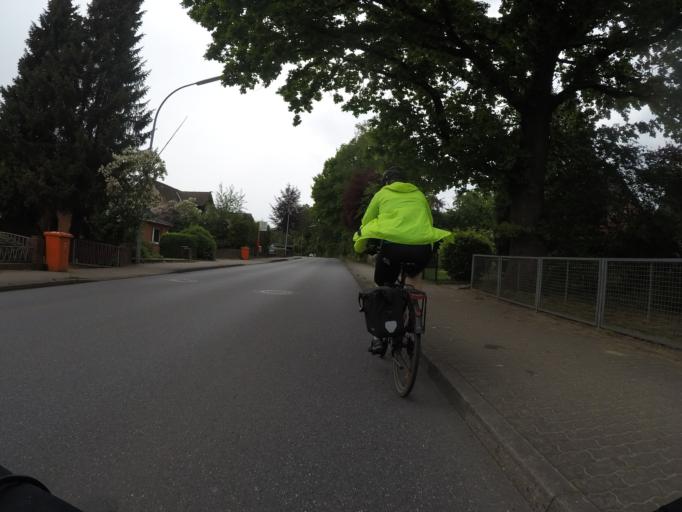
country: DE
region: Schleswig-Holstein
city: Kisdorf
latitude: 53.7929
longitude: 10.0064
